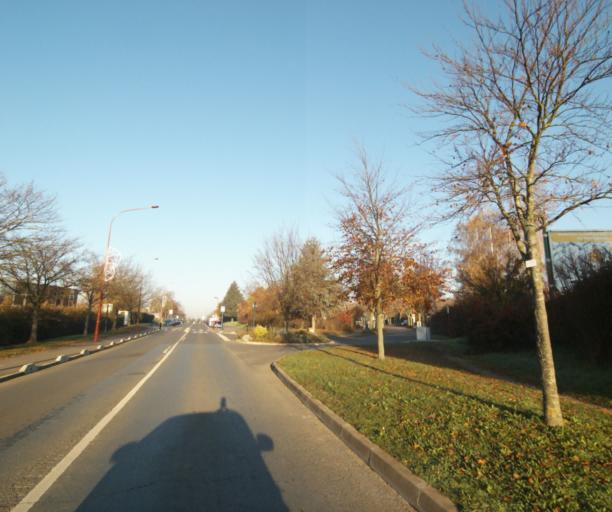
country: FR
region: Ile-de-France
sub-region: Departement du Val-d'Oise
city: Gonesse
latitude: 48.9914
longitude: 2.4454
